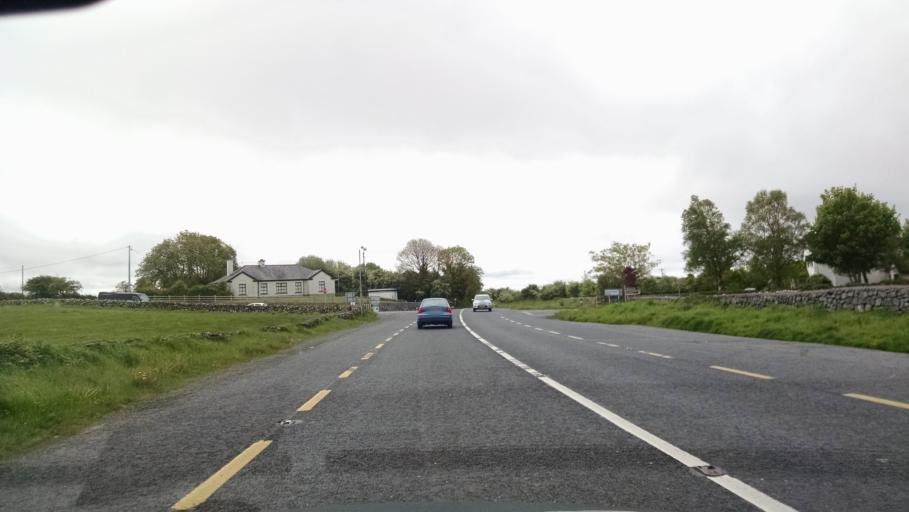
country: IE
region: Connaught
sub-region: County Galway
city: Claregalway
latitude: 53.4044
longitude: -9.0171
